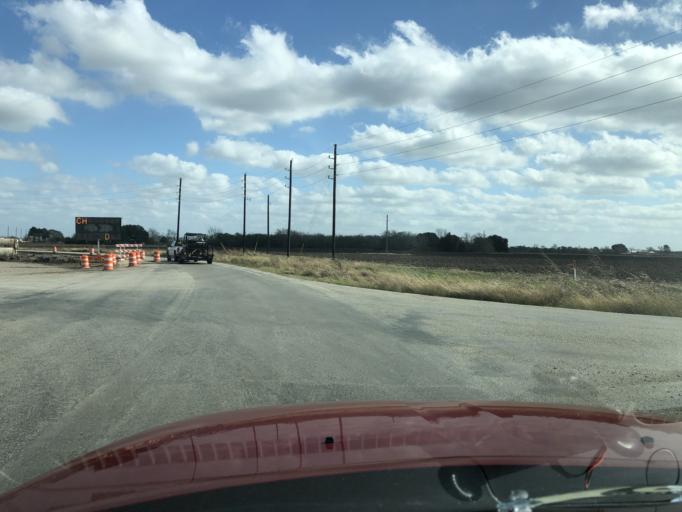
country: US
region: Texas
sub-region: Austin County
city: Sealy
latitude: 29.7722
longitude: -96.0772
